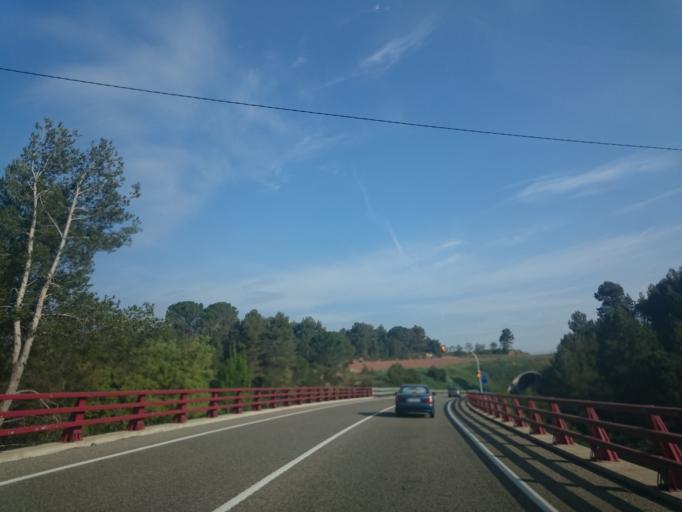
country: ES
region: Catalonia
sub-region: Provincia de Barcelona
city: Sant Salvador de Guardiola
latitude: 41.6794
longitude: 1.7539
